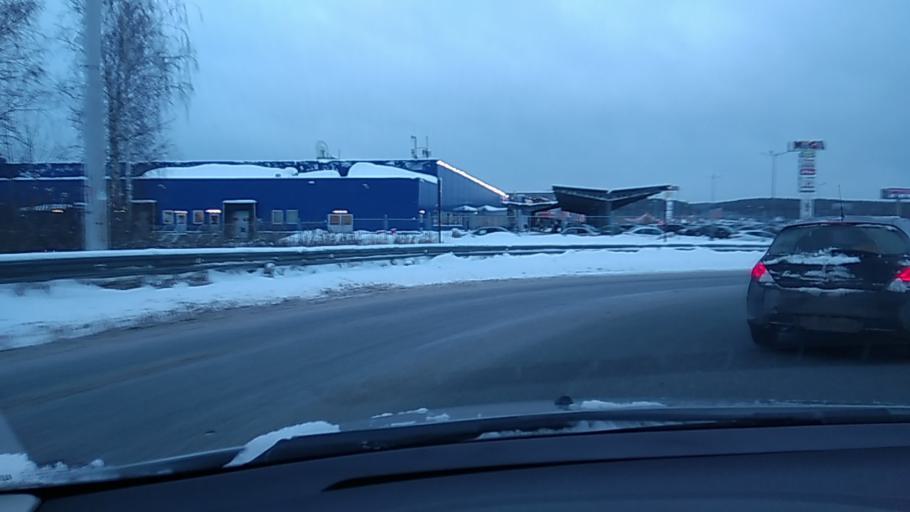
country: RU
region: Sverdlovsk
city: Shirokaya Rechka
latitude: 56.8250
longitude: 60.5135
